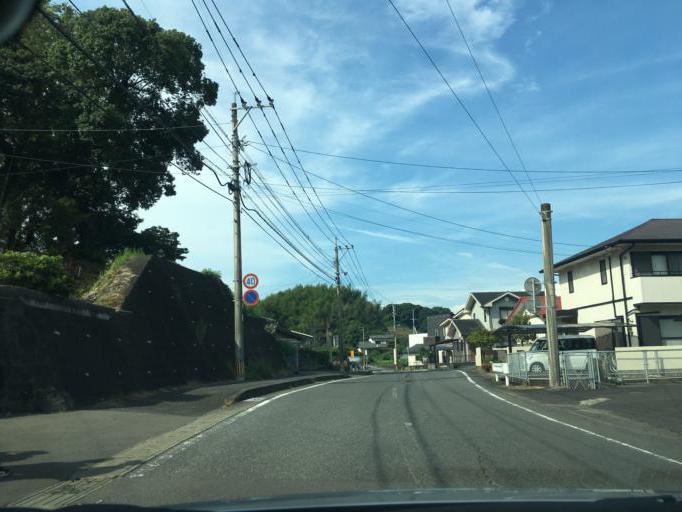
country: JP
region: Saga Prefecture
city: Takeocho-takeo
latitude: 33.1881
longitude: 130.0324
